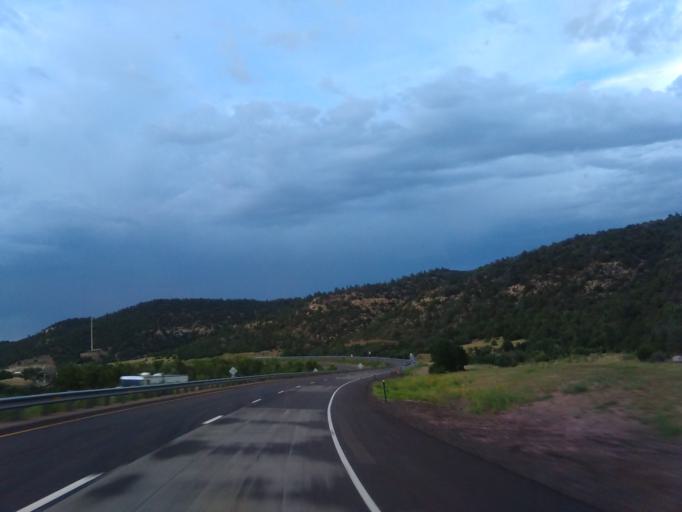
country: US
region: Colorado
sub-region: Las Animas County
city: Trinidad
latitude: 37.0892
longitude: -104.5219
